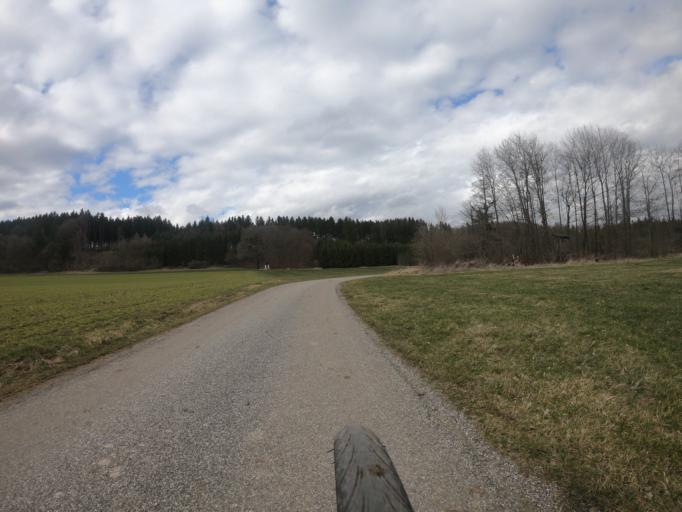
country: DE
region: Bavaria
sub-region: Upper Bavaria
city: Schongeising
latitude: 48.1669
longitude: 11.2013
